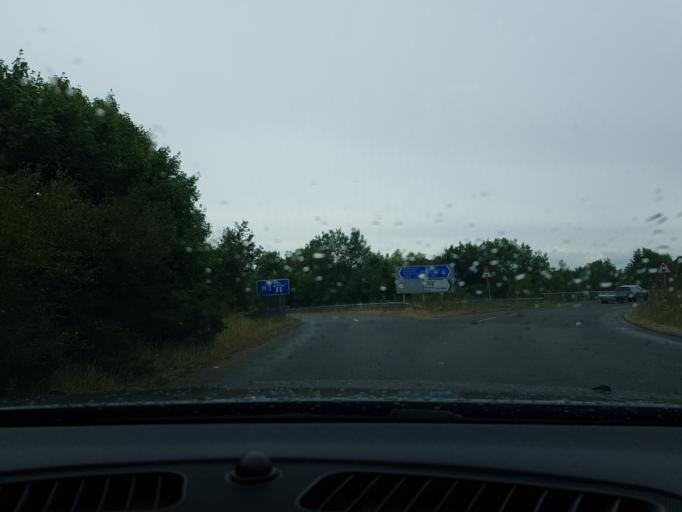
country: GB
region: England
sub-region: Hampshire
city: Hook
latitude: 51.2703
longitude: -0.9603
